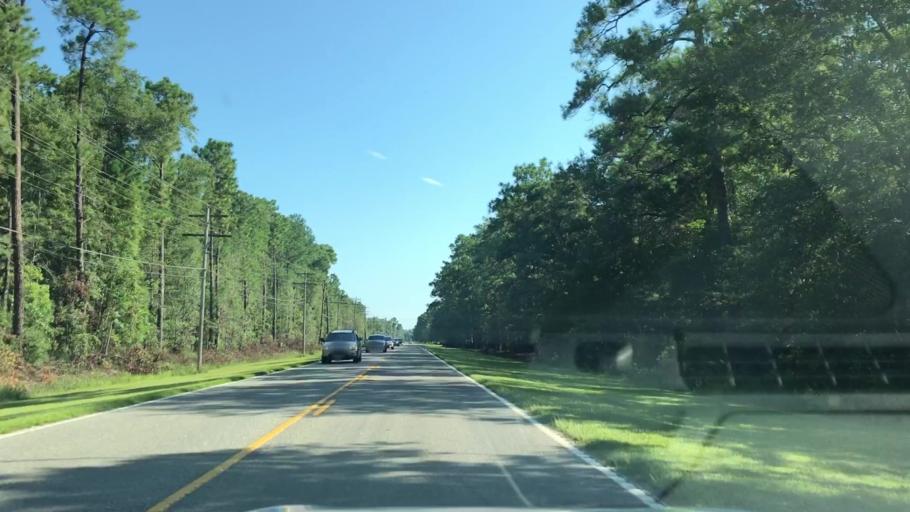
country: US
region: South Carolina
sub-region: Georgetown County
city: Georgetown
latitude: 33.4224
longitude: -79.2819
